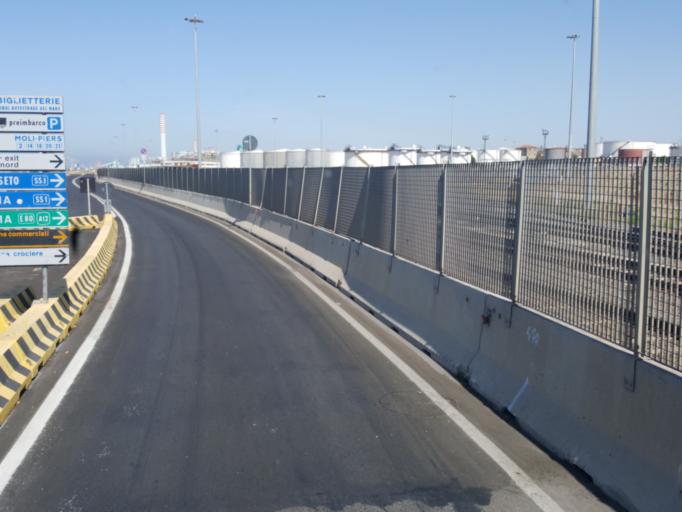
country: IT
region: Latium
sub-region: Citta metropolitana di Roma Capitale
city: Civitavecchia
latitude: 42.1036
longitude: 11.7815
